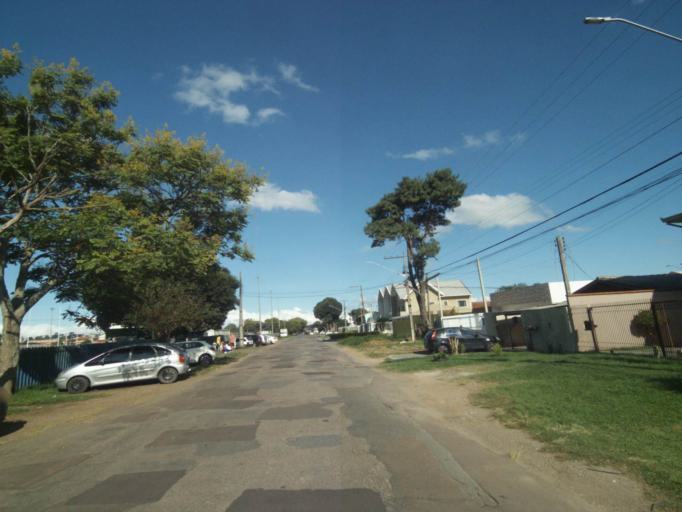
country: BR
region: Parana
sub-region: Pinhais
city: Pinhais
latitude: -25.4359
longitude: -49.2090
